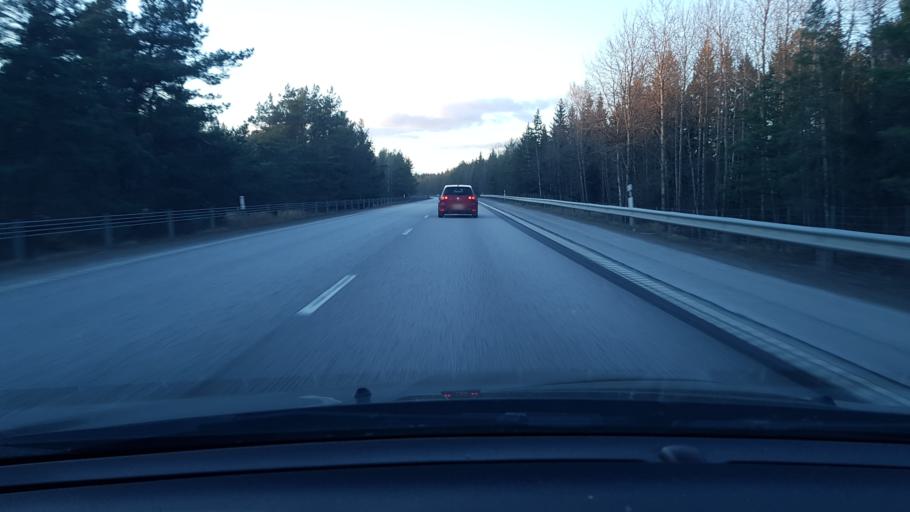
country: SE
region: Uppsala
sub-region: Knivsta Kommun
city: Knivsta
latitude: 59.7546
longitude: 17.8075
